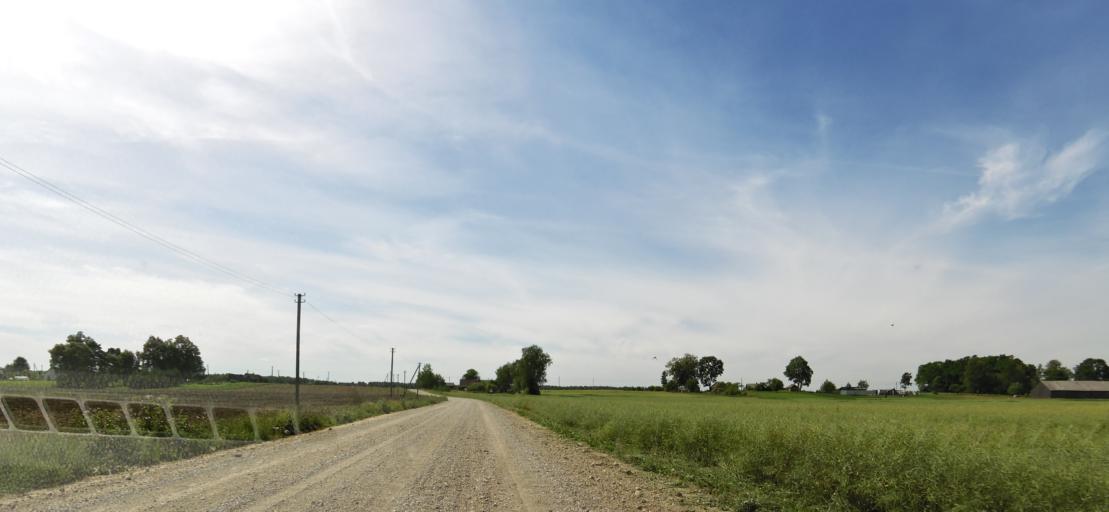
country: LT
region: Panevezys
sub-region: Panevezys City
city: Panevezys
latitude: 55.8843
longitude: 24.3353
